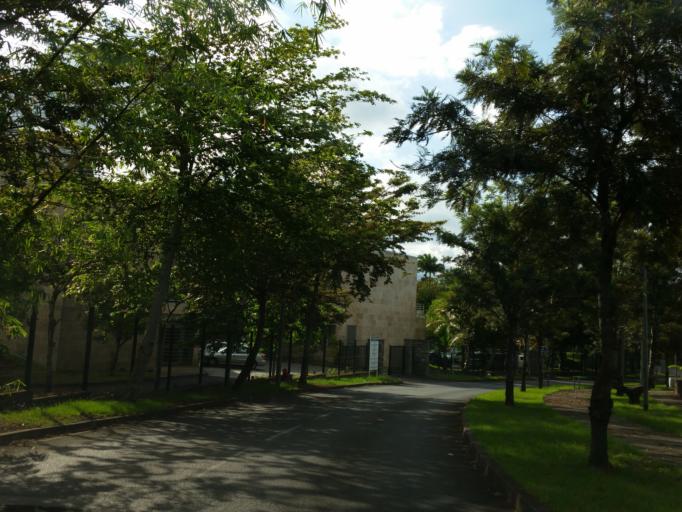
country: RE
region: Reunion
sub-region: Reunion
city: Sainte-Marie
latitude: -20.9066
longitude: 55.4991
